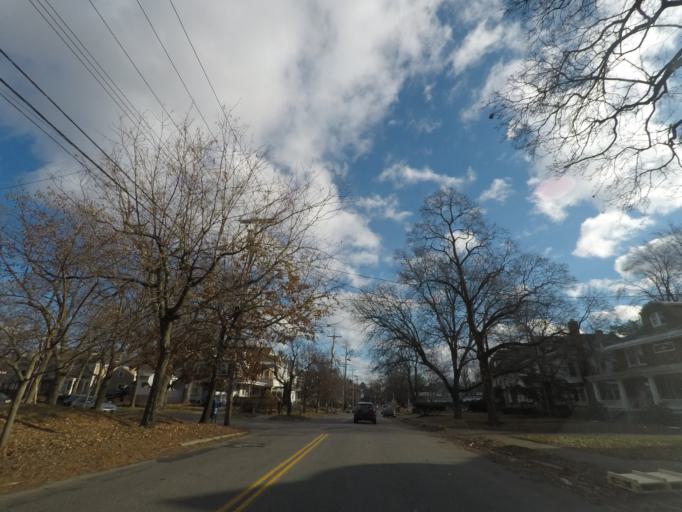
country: US
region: New York
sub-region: Schenectady County
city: Schenectady
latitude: 42.8092
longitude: -73.9164
